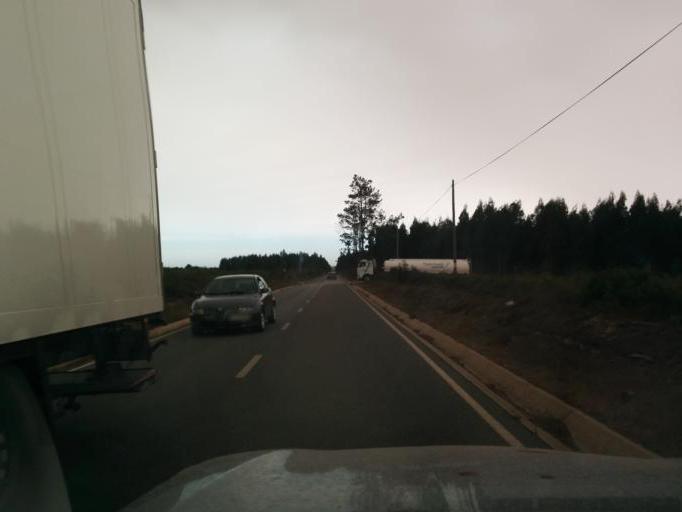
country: PT
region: Beja
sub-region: Odemira
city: Sao Teotonio
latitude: 37.5565
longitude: -8.7351
